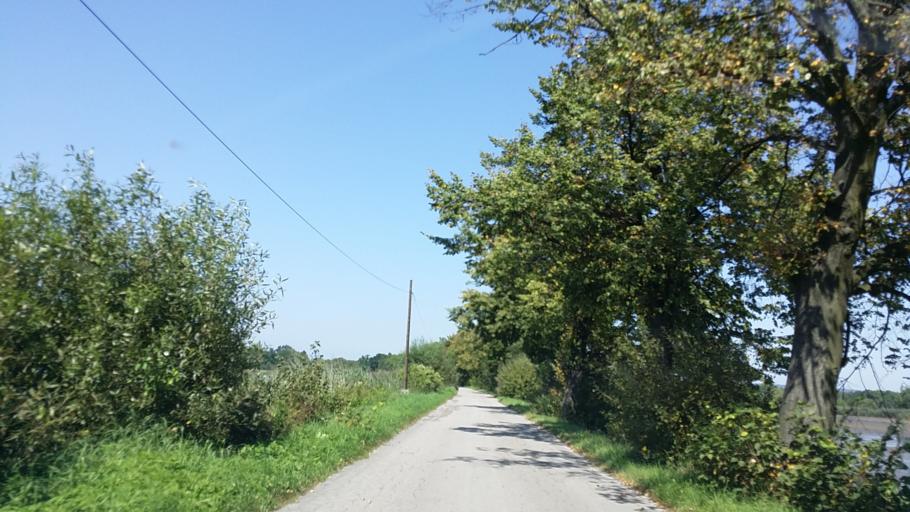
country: PL
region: Lesser Poland Voivodeship
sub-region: Powiat oswiecimski
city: Przeciszow
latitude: 50.0089
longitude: 19.4047
